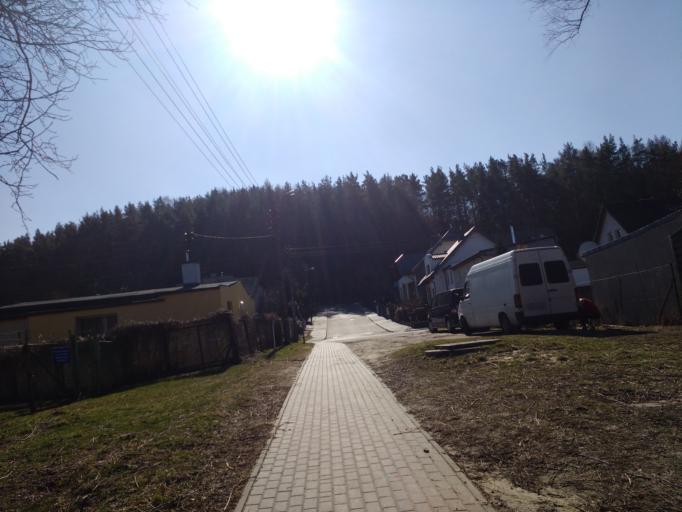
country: PL
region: Pomeranian Voivodeship
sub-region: Gdynia
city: Wielki Kack
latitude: 54.4840
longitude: 18.5189
